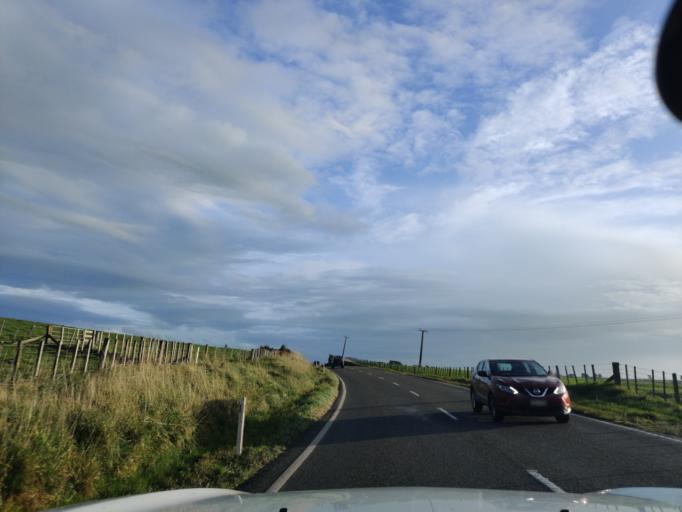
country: NZ
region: Manawatu-Wanganui
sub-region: Palmerston North City
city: Palmerston North
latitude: -40.4986
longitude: 175.4900
